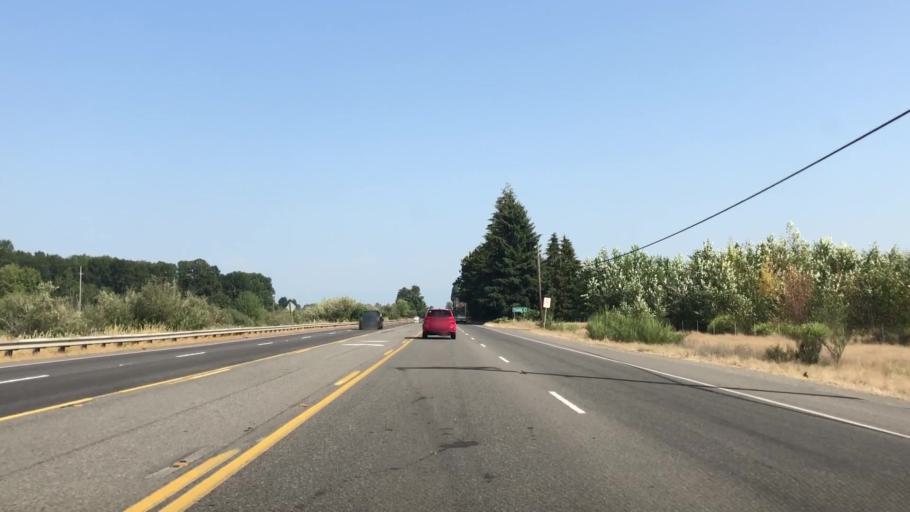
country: US
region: Washington
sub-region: Pierce County
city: Fife
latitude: 47.2327
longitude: -122.3849
